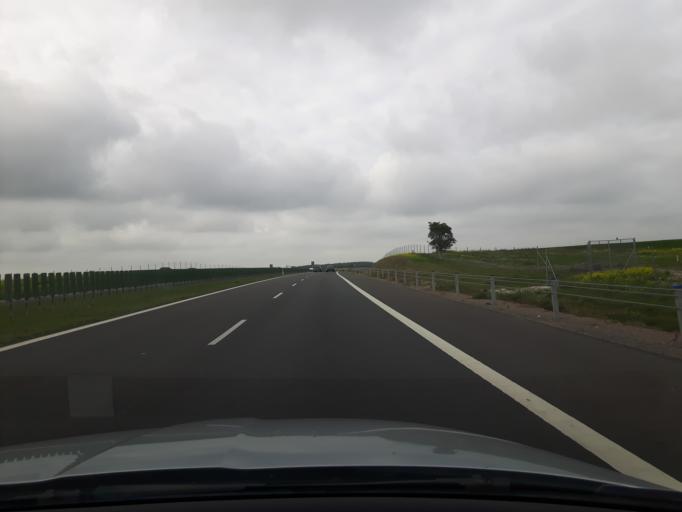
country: PL
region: Swietokrzyskie
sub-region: Powiat jedrzejowski
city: Sobkow
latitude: 50.6982
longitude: 20.3938
